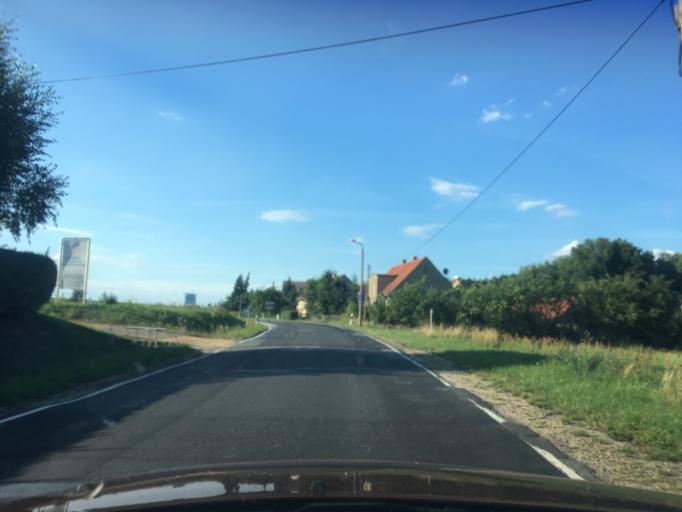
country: DE
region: Saxony
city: Goerlitz
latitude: 51.2072
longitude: 14.9993
